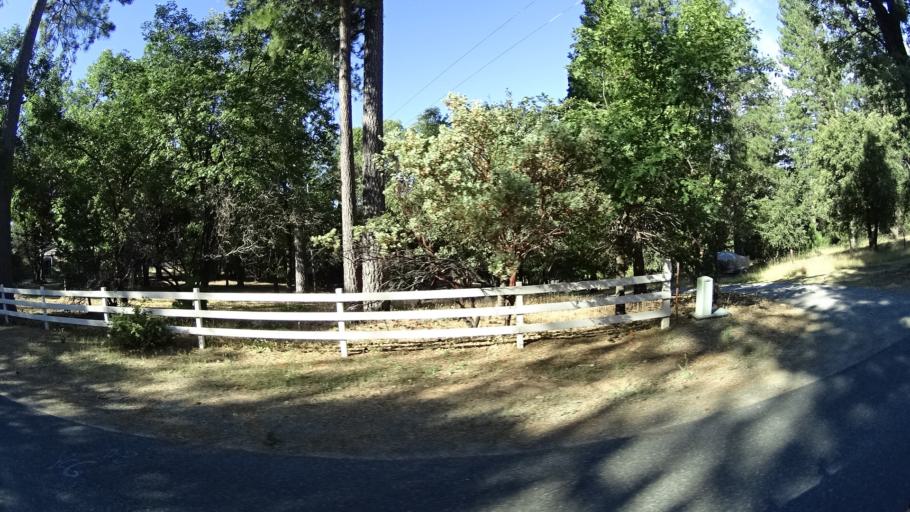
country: US
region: California
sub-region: Amador County
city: Pioneer
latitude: 38.3878
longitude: -120.5460
